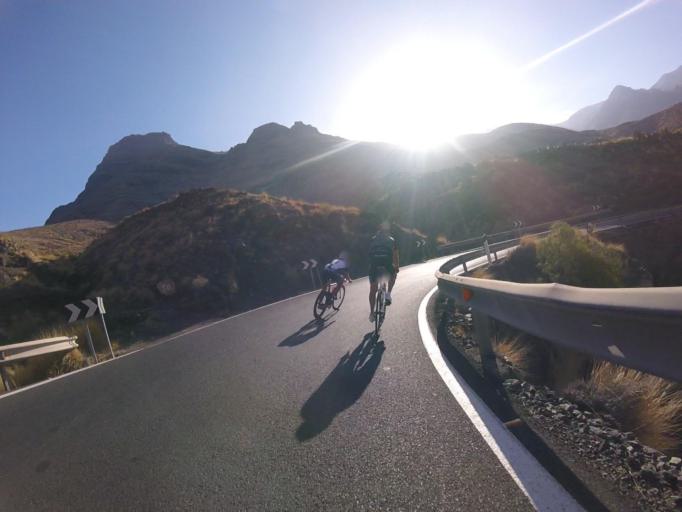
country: ES
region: Canary Islands
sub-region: Provincia de Las Palmas
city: Agaete
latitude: 28.0532
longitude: -15.7314
